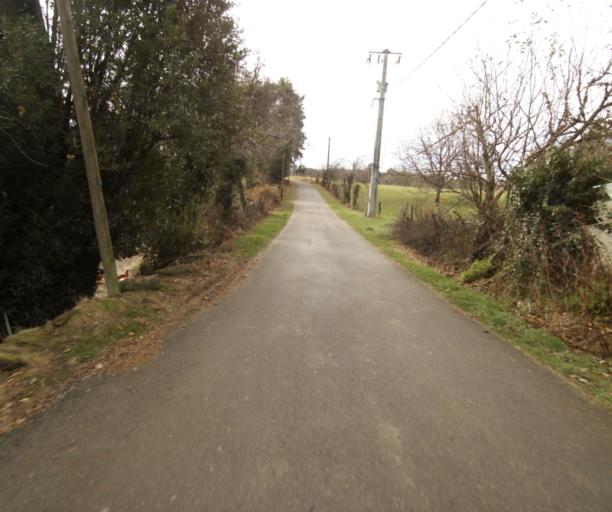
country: FR
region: Limousin
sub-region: Departement de la Correze
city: Chameyrat
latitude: 45.2557
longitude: 1.6856
